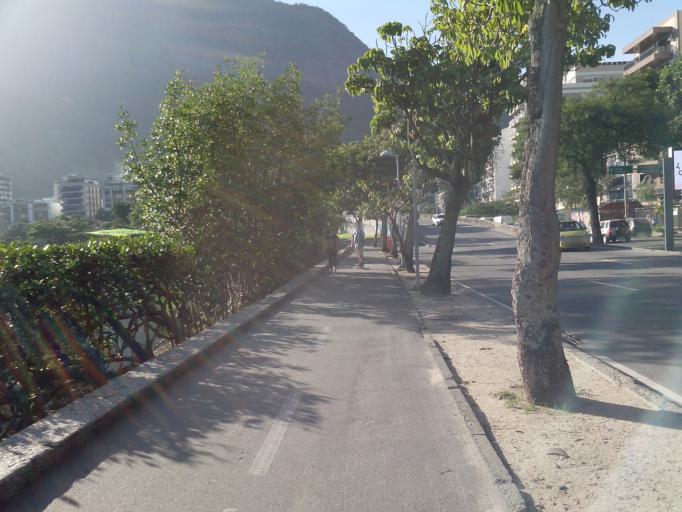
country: BR
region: Rio de Janeiro
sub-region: Rio De Janeiro
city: Rio de Janeiro
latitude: -22.9646
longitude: -43.2038
